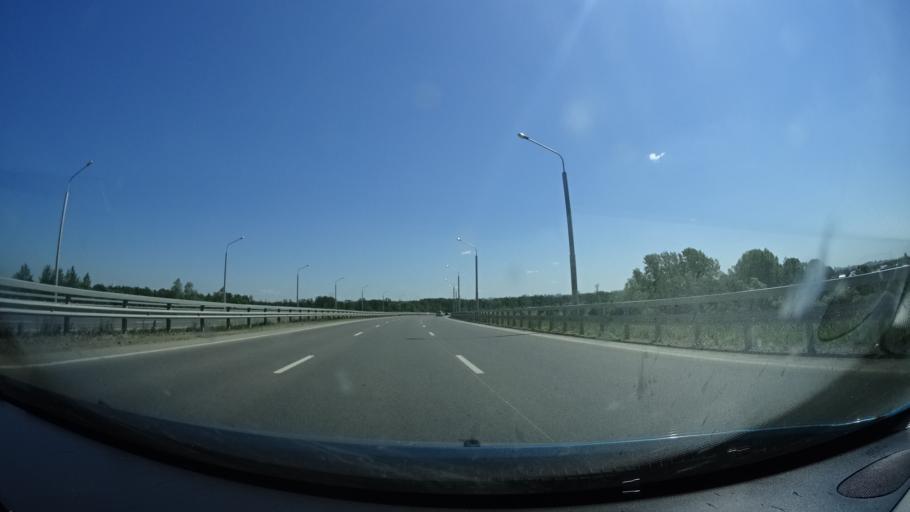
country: RU
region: Bashkortostan
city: Mikhaylovka
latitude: 54.7972
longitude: 55.8928
